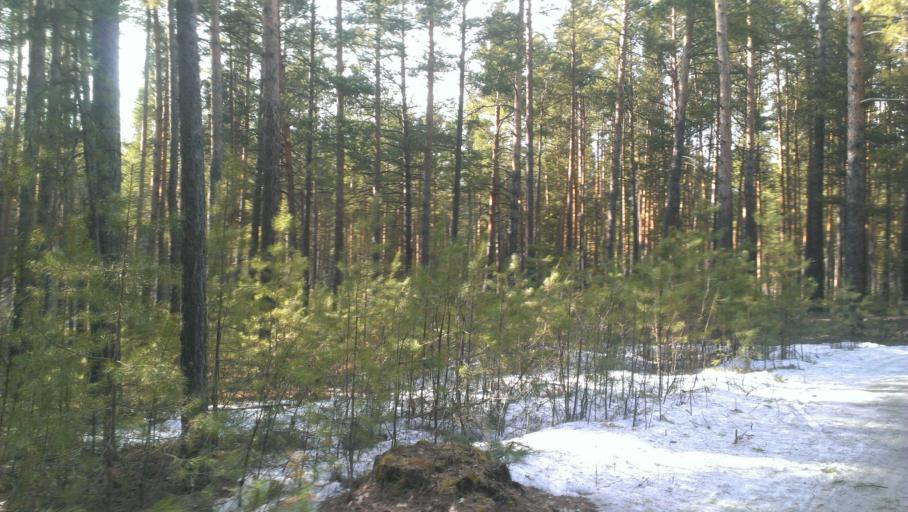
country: RU
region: Altai Krai
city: Yuzhnyy
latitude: 53.2840
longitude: 83.6991
